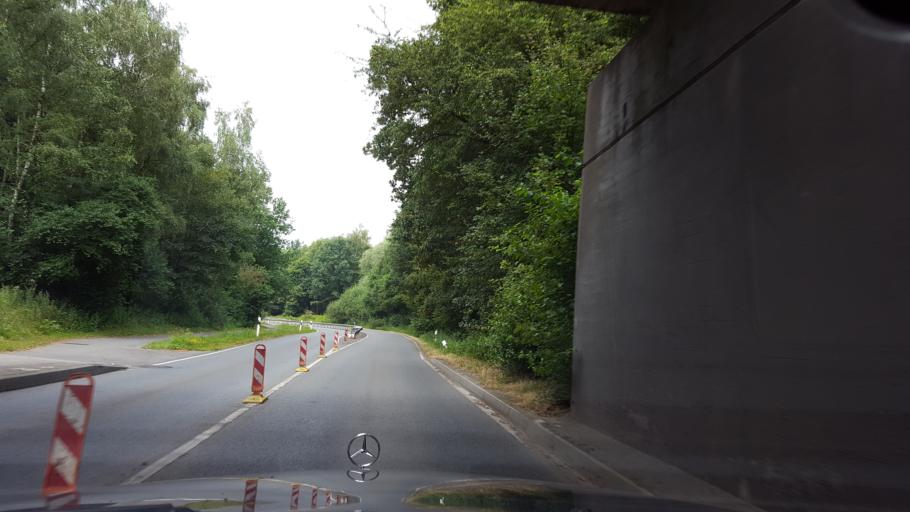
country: DE
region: North Rhine-Westphalia
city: Marl
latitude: 51.6911
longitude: 7.1410
